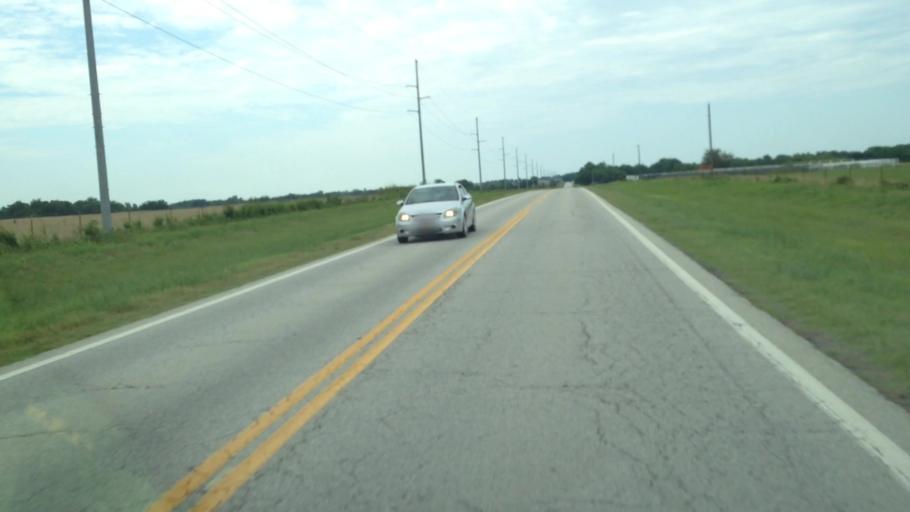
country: US
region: Kansas
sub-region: Labette County
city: Chetopa
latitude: 36.9193
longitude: -95.0896
